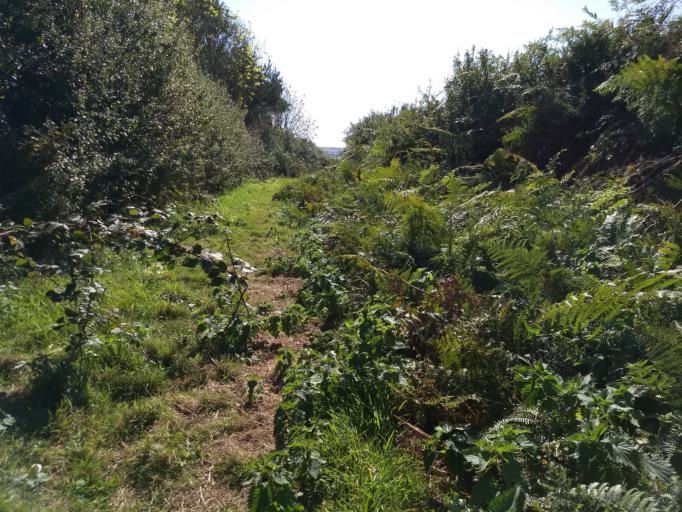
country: GB
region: England
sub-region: Isle of Wight
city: Niton
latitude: 50.6320
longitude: -1.2800
